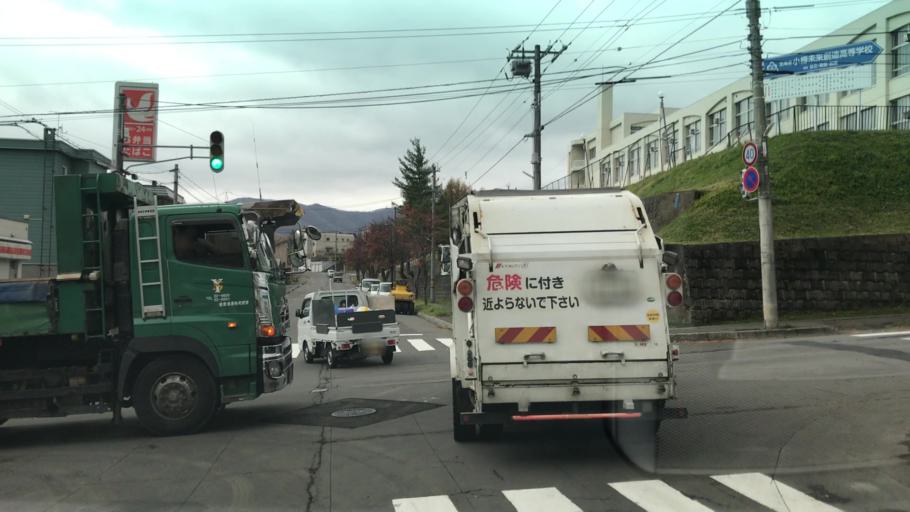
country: JP
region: Hokkaido
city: Otaru
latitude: 43.1817
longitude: 140.9825
